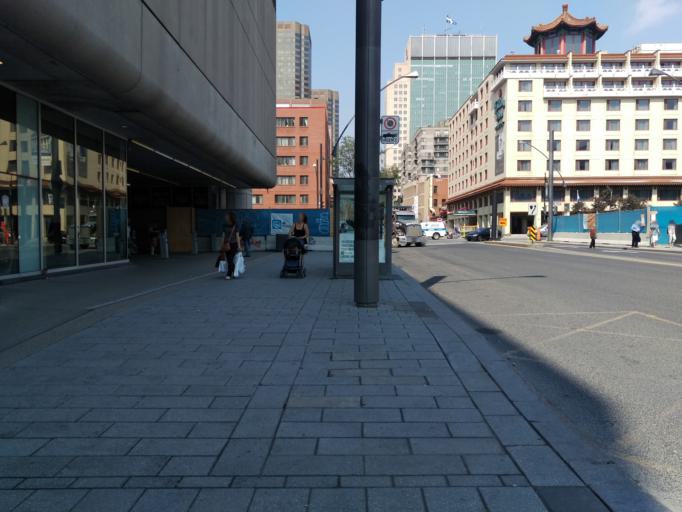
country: CA
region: Quebec
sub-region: Montreal
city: Montreal
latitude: 45.5059
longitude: -73.5592
